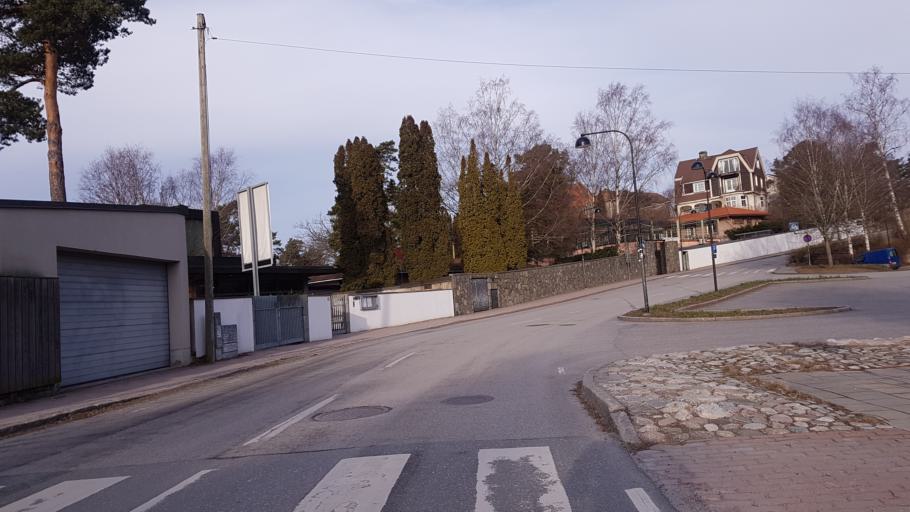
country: SE
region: Stockholm
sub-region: Lidingo
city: Lidingoe
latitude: 59.3587
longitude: 18.1234
